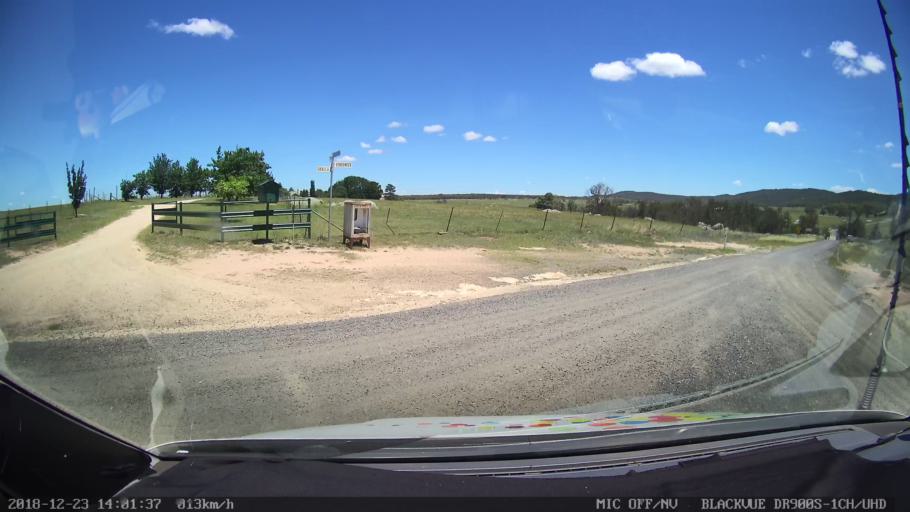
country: AU
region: New South Wales
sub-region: Tamworth Municipality
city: Manilla
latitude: -30.6215
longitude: 151.1109
